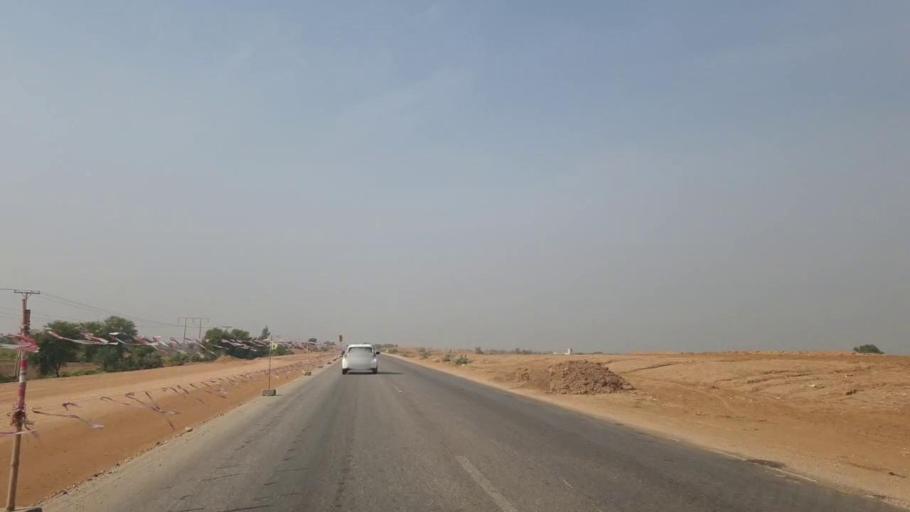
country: PK
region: Sindh
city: Sann
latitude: 26.1280
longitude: 68.0520
